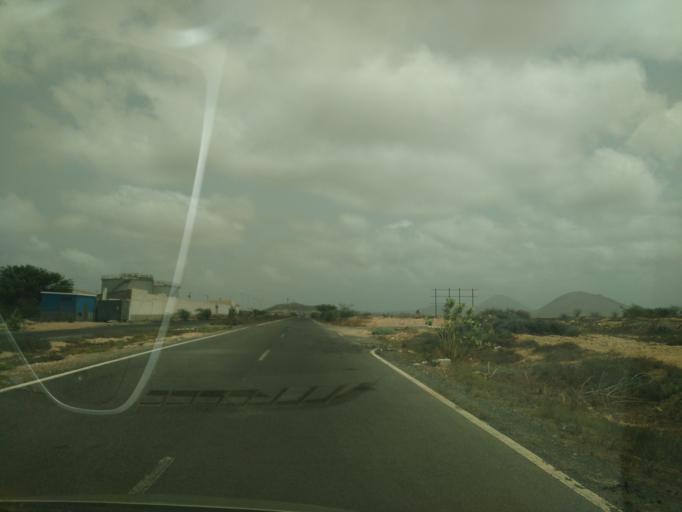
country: CV
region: Sal
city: Espargos
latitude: 16.7304
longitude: -22.9417
